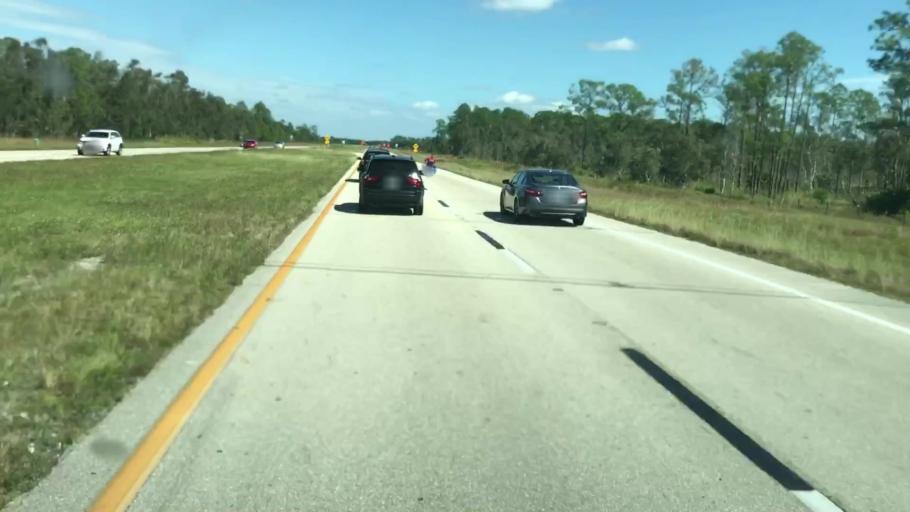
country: US
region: Florida
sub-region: Lee County
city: Gateway
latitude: 26.5653
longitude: -81.7316
